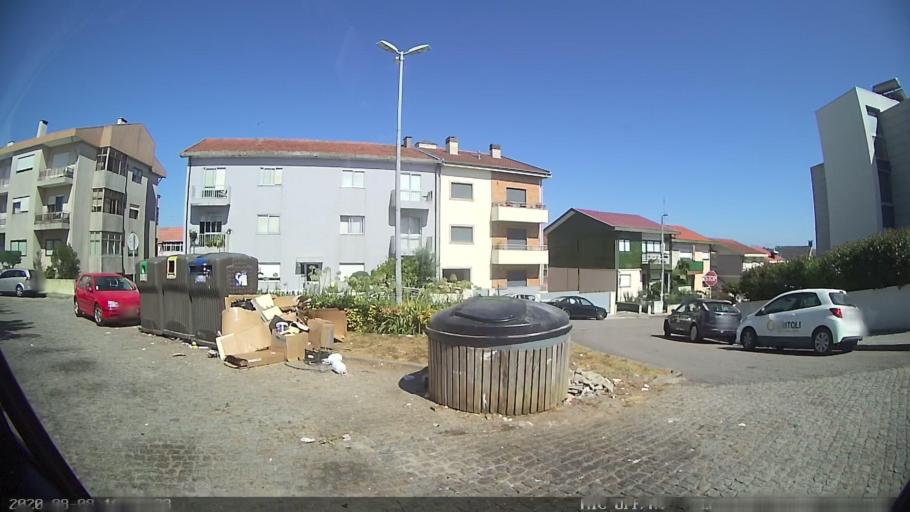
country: PT
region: Porto
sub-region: Valongo
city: Ermesinde
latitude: 41.2058
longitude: -8.5531
